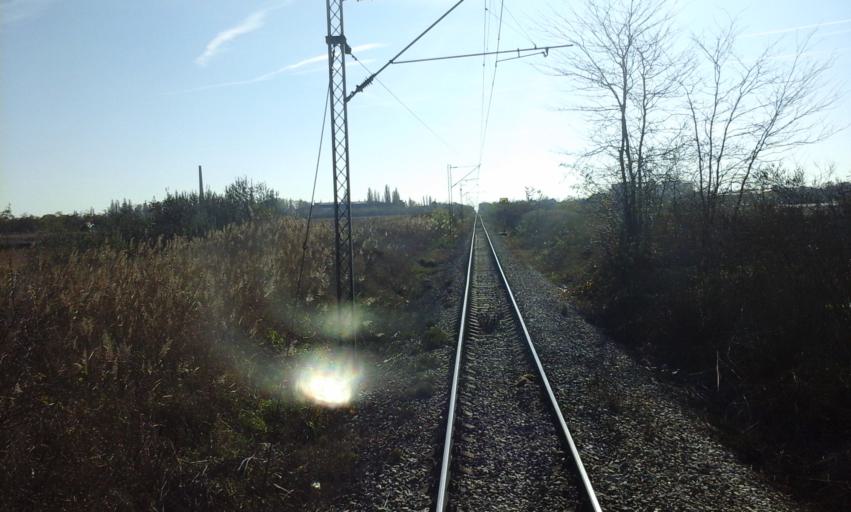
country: RS
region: Autonomna Pokrajina Vojvodina
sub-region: Severnobacki Okrug
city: Subotica
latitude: 46.0760
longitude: 19.6893
